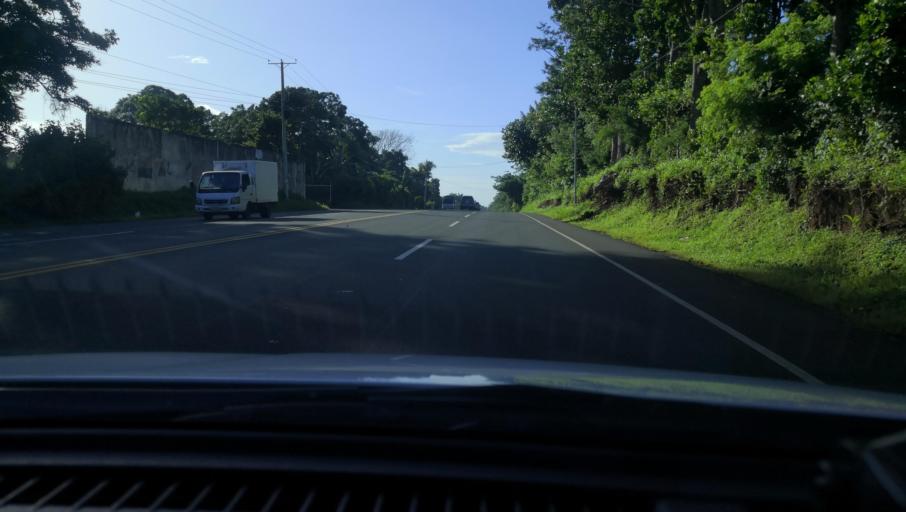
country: NI
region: Carazo
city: La Paz de Oriente
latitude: 11.8237
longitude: -86.1614
